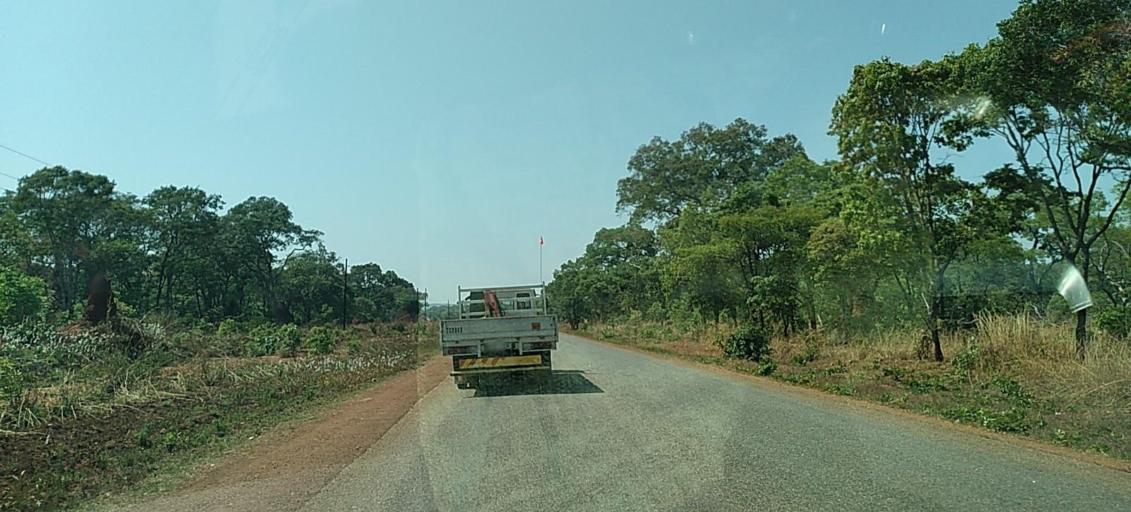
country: ZM
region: North-Western
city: Solwezi
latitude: -12.2077
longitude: 25.5576
